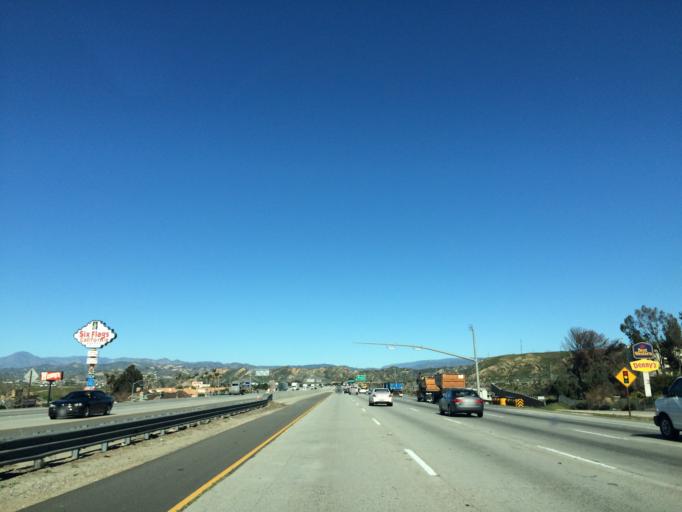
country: US
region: California
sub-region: Los Angeles County
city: Valencia
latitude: 34.4206
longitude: -118.5816
